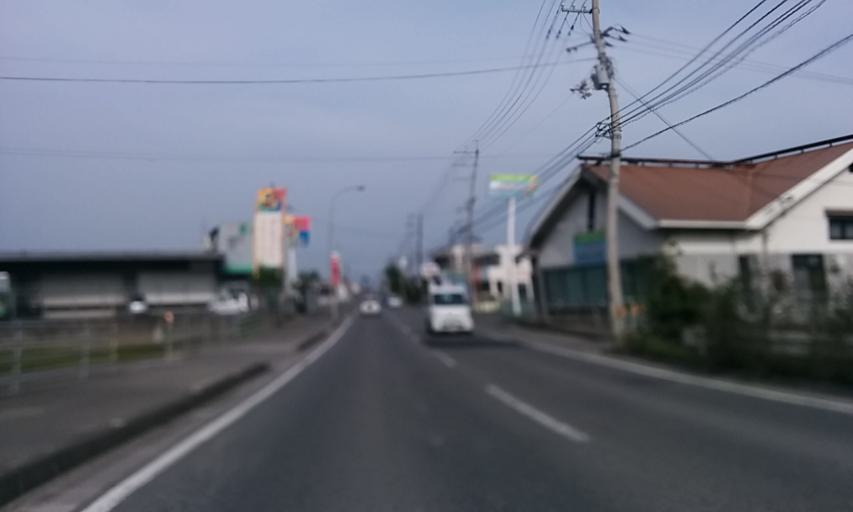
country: JP
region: Ehime
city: Kawanoecho
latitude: 33.9667
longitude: 133.4895
